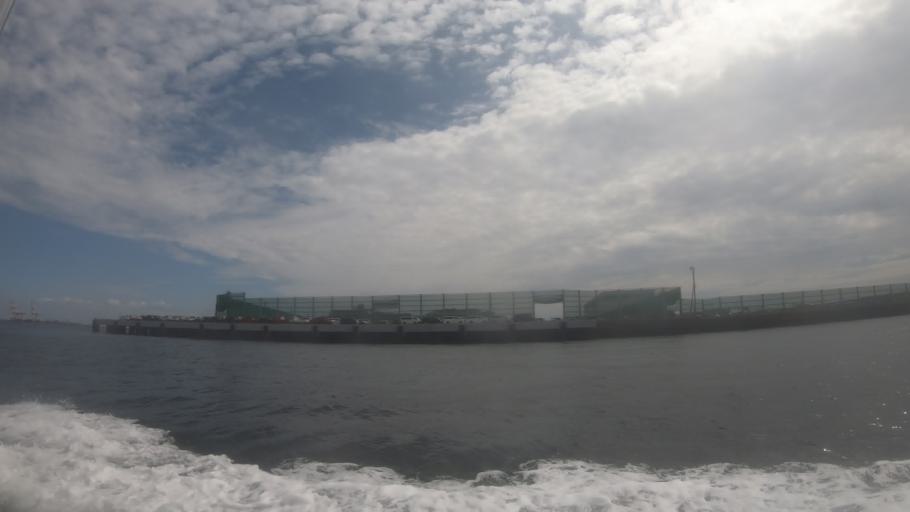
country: JP
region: Kanagawa
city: Yokohama
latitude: 35.3902
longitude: 139.6438
